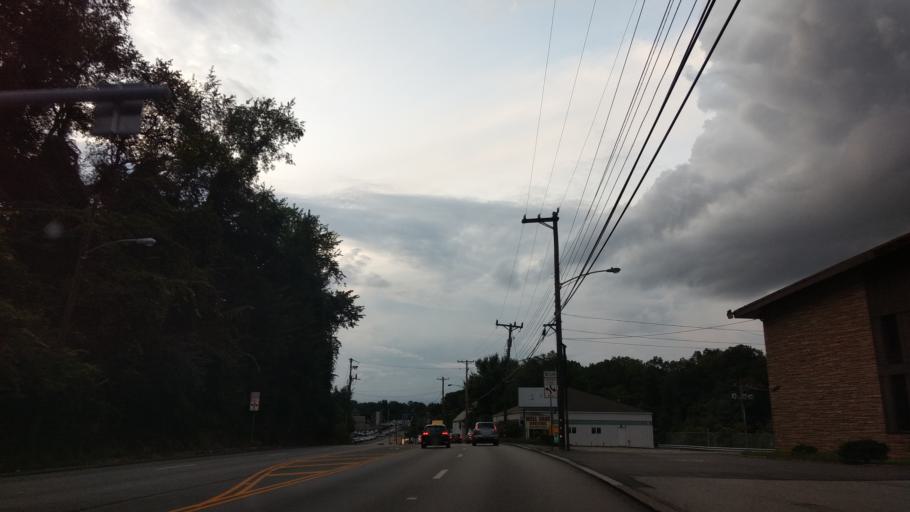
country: US
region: Pennsylvania
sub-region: Allegheny County
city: Baldwin
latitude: 40.3474
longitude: -79.9738
